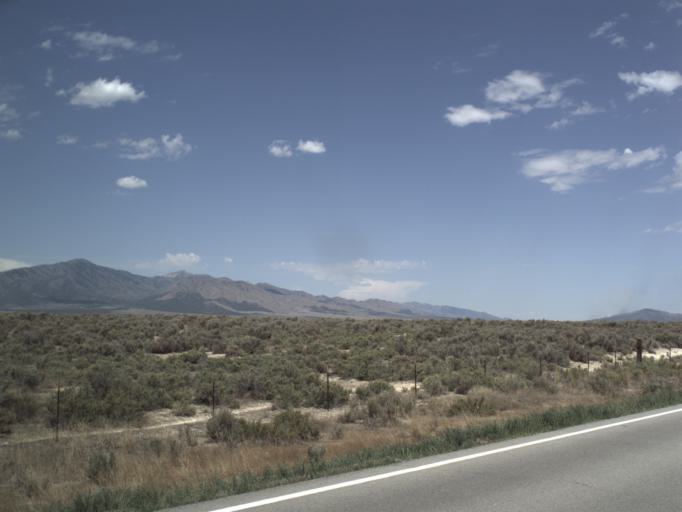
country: US
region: Utah
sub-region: Tooele County
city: Tooele
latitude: 40.2481
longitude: -112.3999
